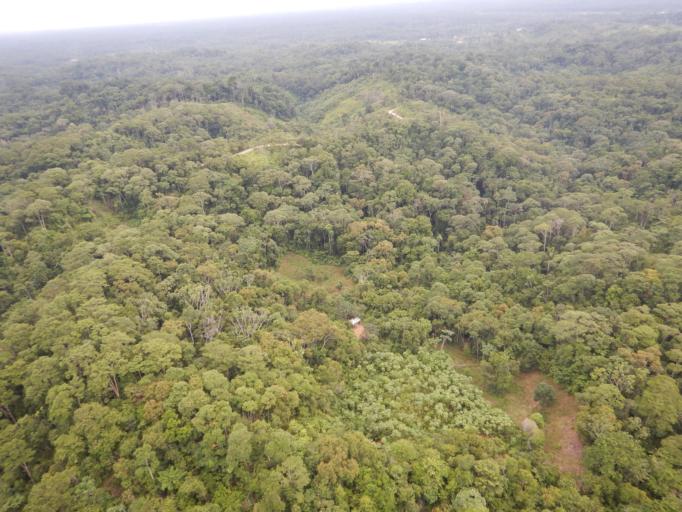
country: BO
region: Cochabamba
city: Chimore
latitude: -17.0458
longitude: -64.9005
